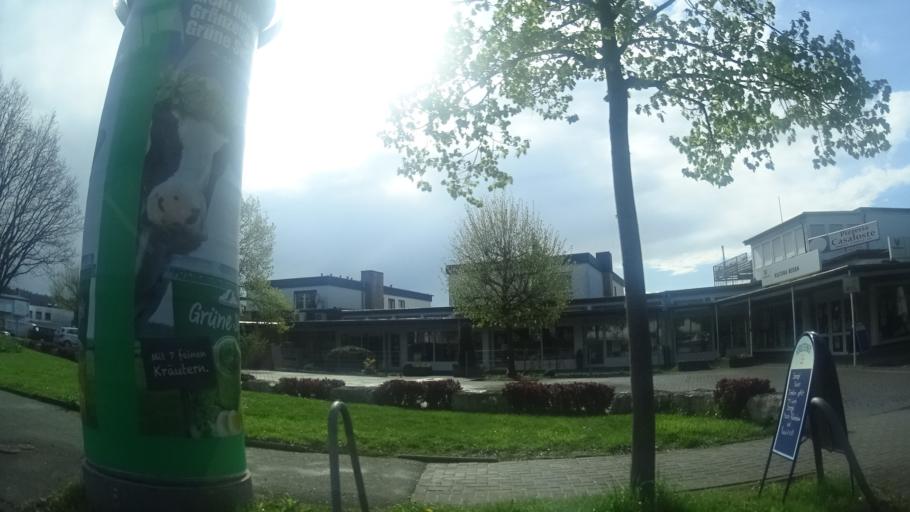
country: DE
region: Hesse
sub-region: Regierungsbezirk Giessen
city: Wetzlar
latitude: 50.5419
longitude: 8.5243
